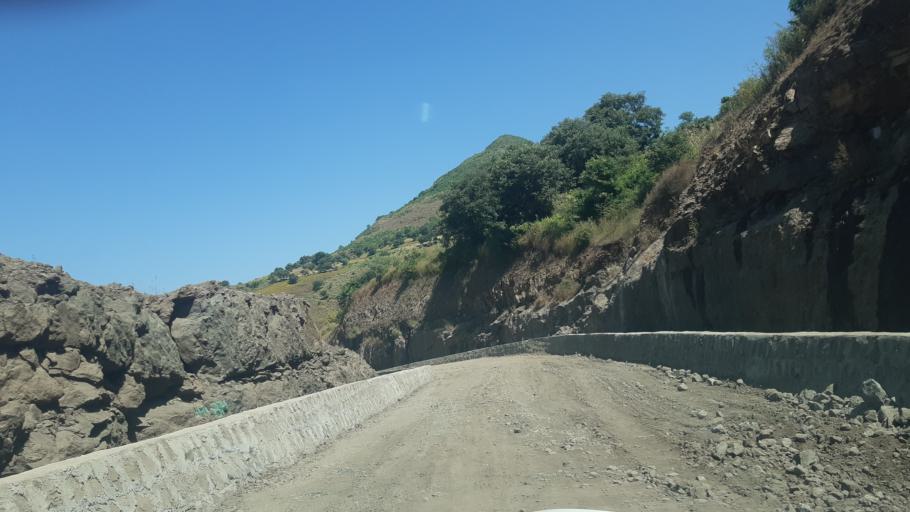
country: ET
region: Amhara
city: Dabat
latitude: 13.1667
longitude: 37.6056
